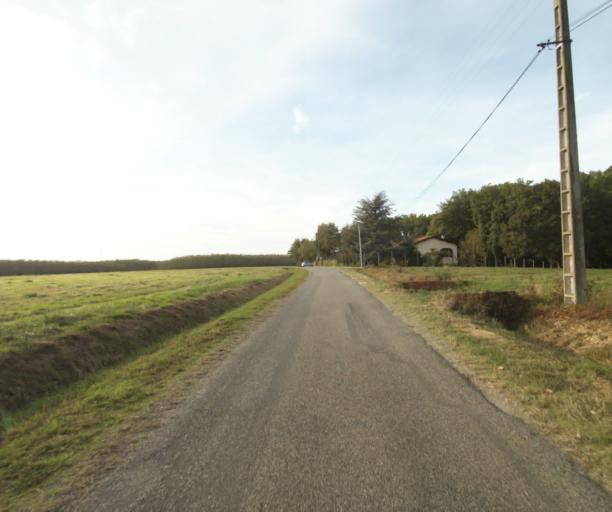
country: FR
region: Midi-Pyrenees
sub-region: Departement du Tarn-et-Garonne
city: Campsas
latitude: 43.8719
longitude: 1.3332
